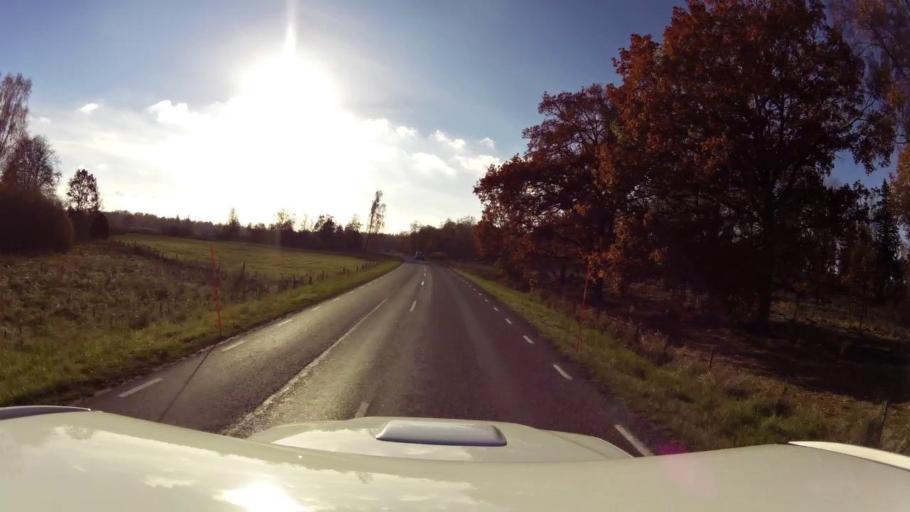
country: SE
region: OEstergoetland
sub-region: Linkopings Kommun
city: Malmslatt
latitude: 58.3449
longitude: 15.5217
